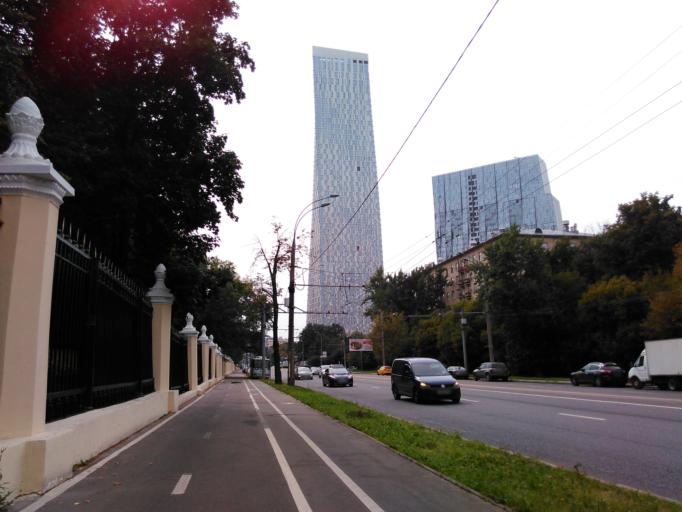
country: RU
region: Moscow
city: Vorob'yovo
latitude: 55.7253
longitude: 37.5329
